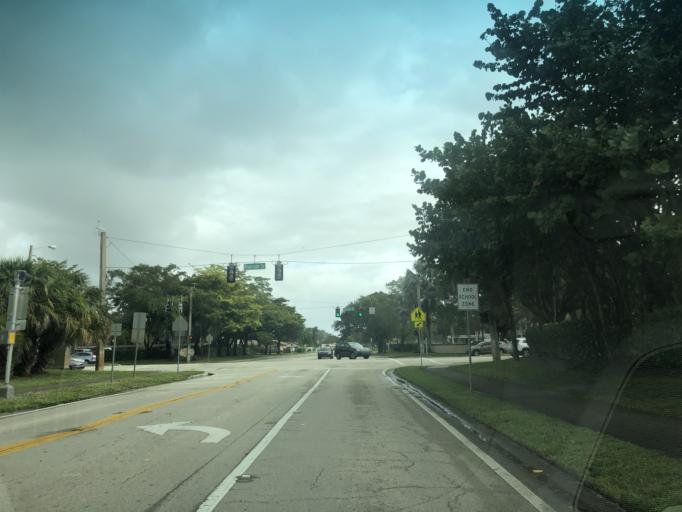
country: US
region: Florida
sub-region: Broward County
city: North Lauderdale
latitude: 26.2469
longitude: -80.2432
